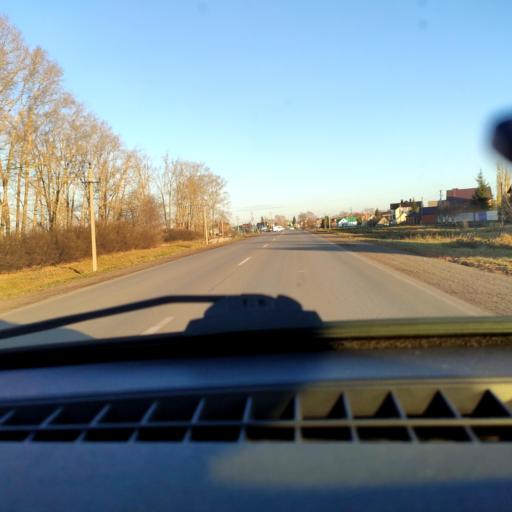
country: RU
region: Bashkortostan
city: Ufa
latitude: 54.6114
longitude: 55.8915
